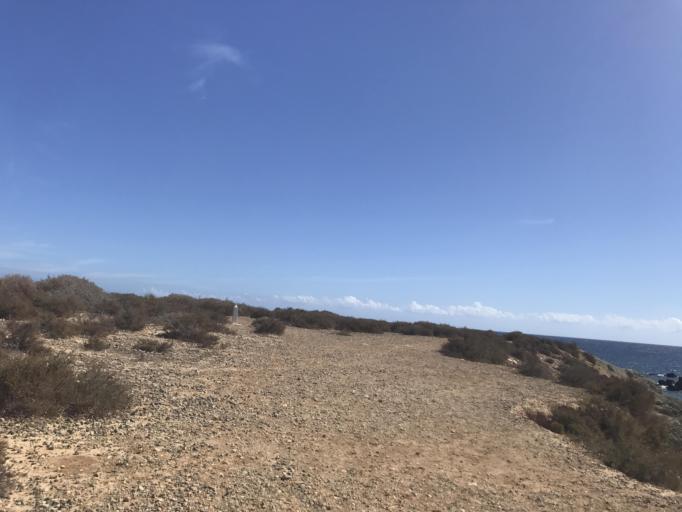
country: ES
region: Valencia
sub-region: Provincia de Alicante
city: Santa Pola
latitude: 38.1627
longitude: -0.4714
